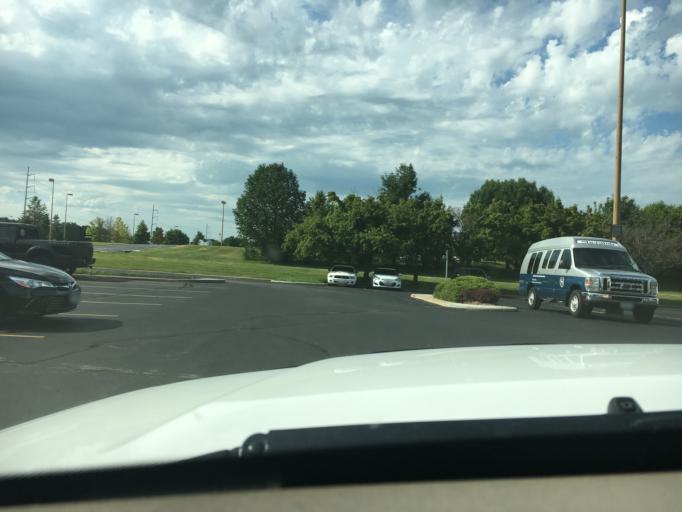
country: US
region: Iowa
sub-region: Polk County
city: Clive
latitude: 41.5989
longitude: -93.7724
